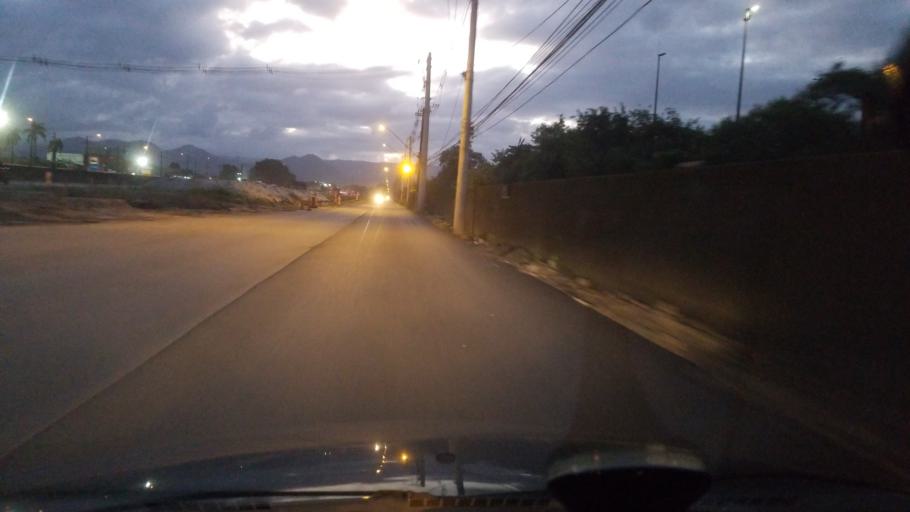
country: BR
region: Sao Paulo
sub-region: Sao Vicente
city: Sao Vicente
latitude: -23.9273
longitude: -46.3716
